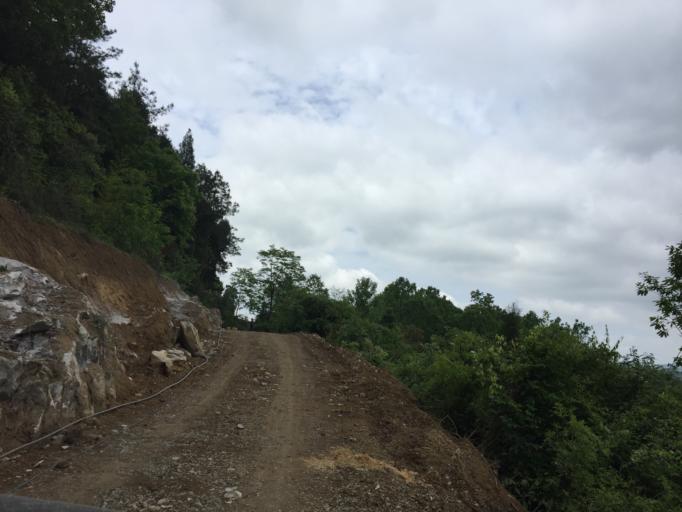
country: CN
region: Guizhou Sheng
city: Kuanping
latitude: 28.0159
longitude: 108.0708
